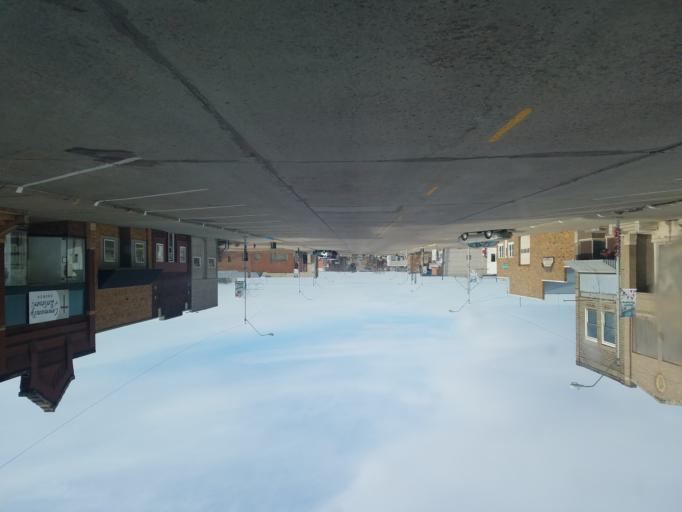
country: US
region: Nebraska
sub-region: Knox County
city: Creighton
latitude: 42.4666
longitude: -97.9061
